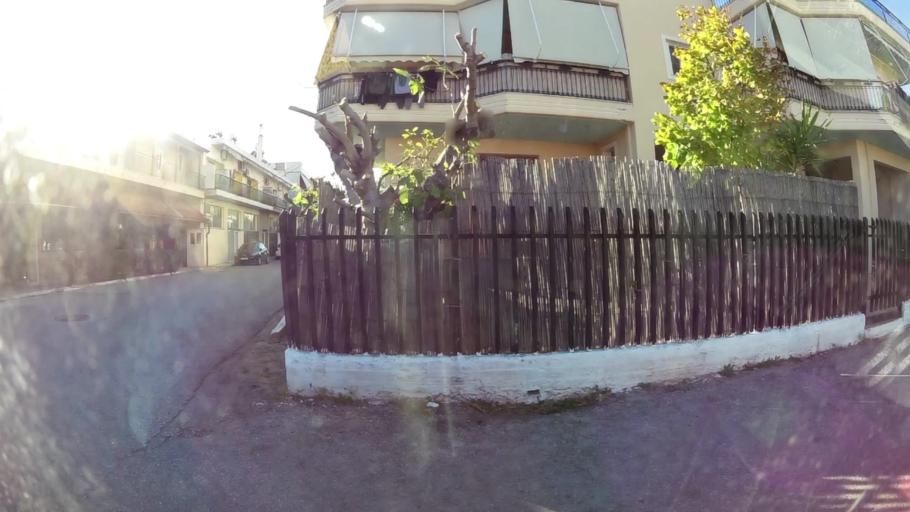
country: GR
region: Attica
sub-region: Nomarchia Anatolikis Attikis
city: Acharnes
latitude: 38.0908
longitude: 23.7330
